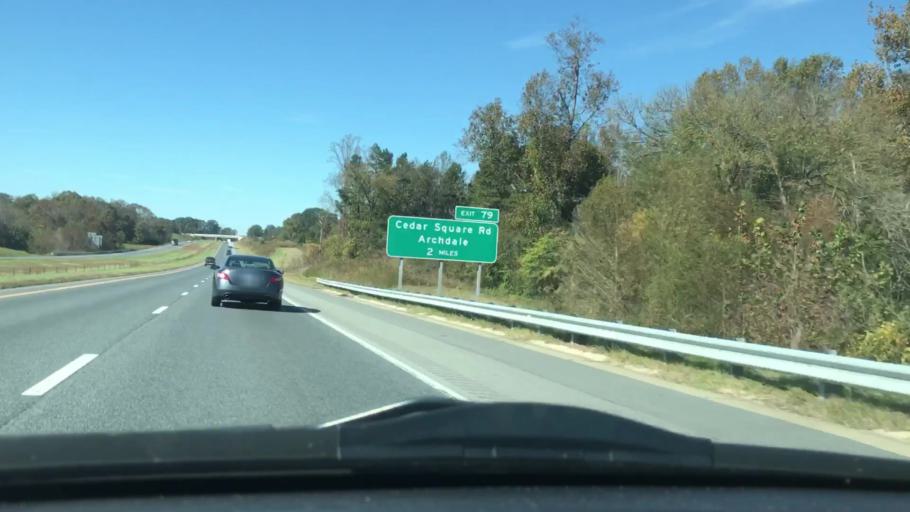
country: US
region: North Carolina
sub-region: Randolph County
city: Randleman
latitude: 35.8487
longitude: -79.8723
